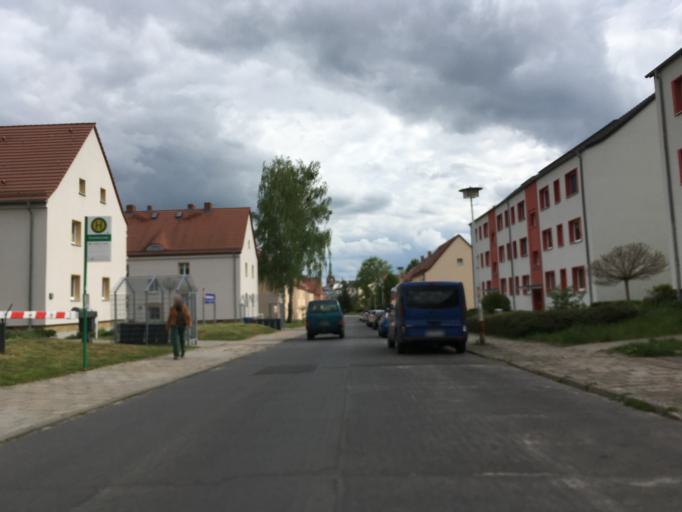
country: DE
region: Brandenburg
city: Bernau bei Berlin
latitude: 52.6835
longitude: 13.5916
